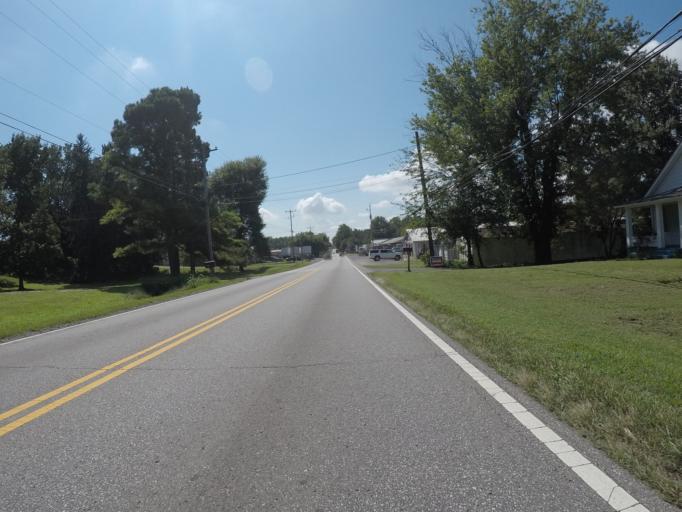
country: US
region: Ohio
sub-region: Lawrence County
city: South Point
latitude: 38.4491
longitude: -82.5939
